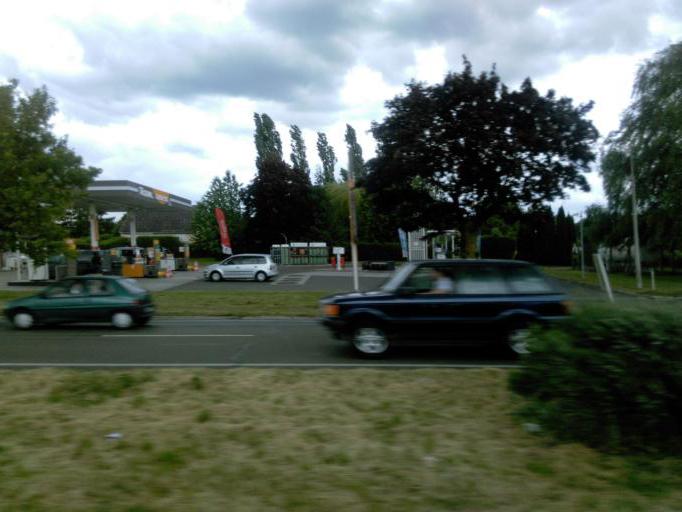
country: FR
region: Ile-de-France
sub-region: Departement du Val-d'Oise
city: Osny
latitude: 49.0819
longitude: 2.0691
